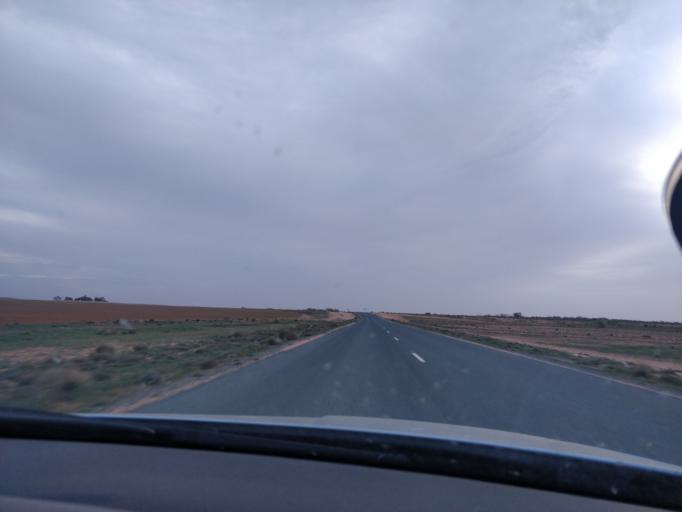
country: AU
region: New South Wales
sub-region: Wentworth
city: Gol Gol
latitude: -34.0475
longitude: 142.3313
